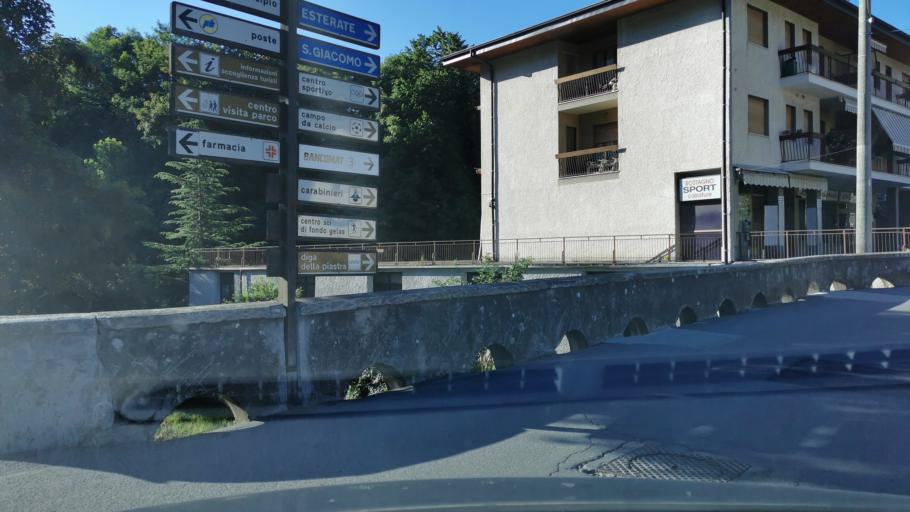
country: IT
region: Piedmont
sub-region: Provincia di Cuneo
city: Entracque
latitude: 44.2396
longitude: 7.3975
